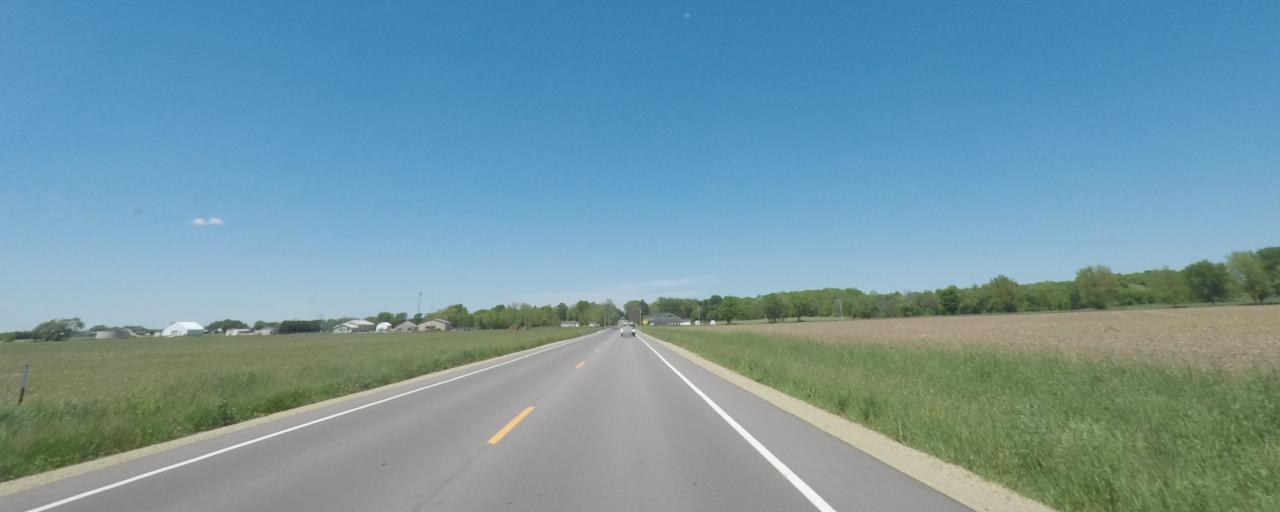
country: US
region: Wisconsin
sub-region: Green County
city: Brooklyn
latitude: 42.8424
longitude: -89.3692
